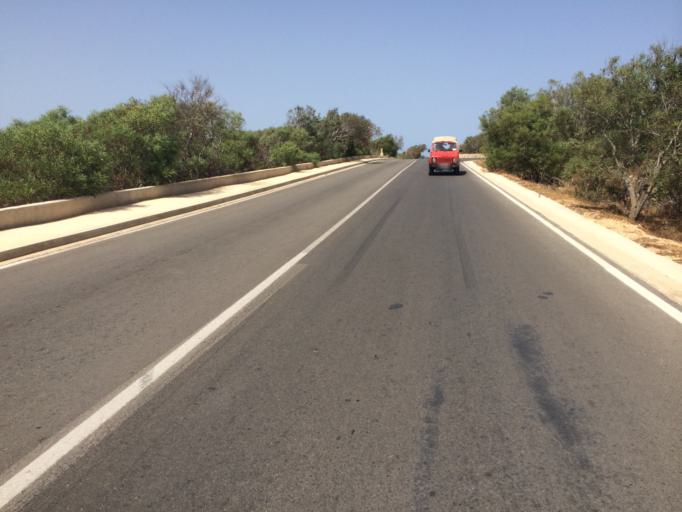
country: MT
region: Il-Mellieha
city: Mellieha
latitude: 35.9778
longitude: 14.3501
